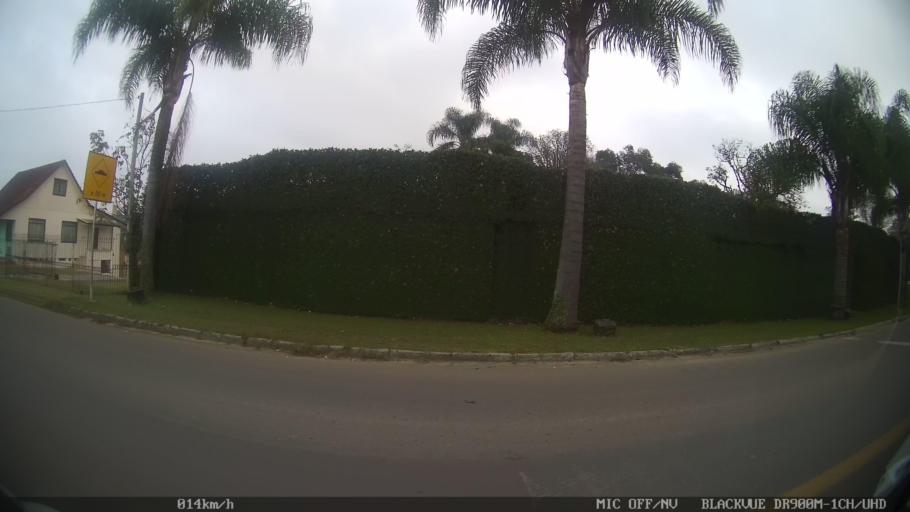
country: BR
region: Parana
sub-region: Almirante Tamandare
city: Almirante Tamandare
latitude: -25.3729
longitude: -49.3197
